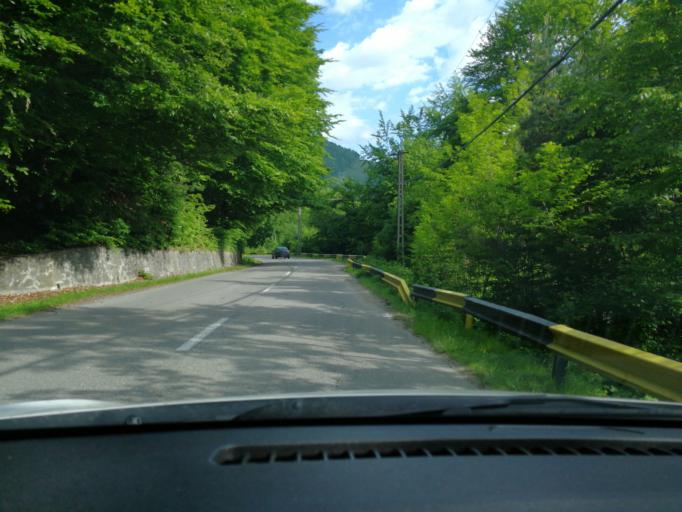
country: RO
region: Prahova
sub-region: Comuna Sotrile
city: Sotrile
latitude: 45.2570
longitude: 25.7384
